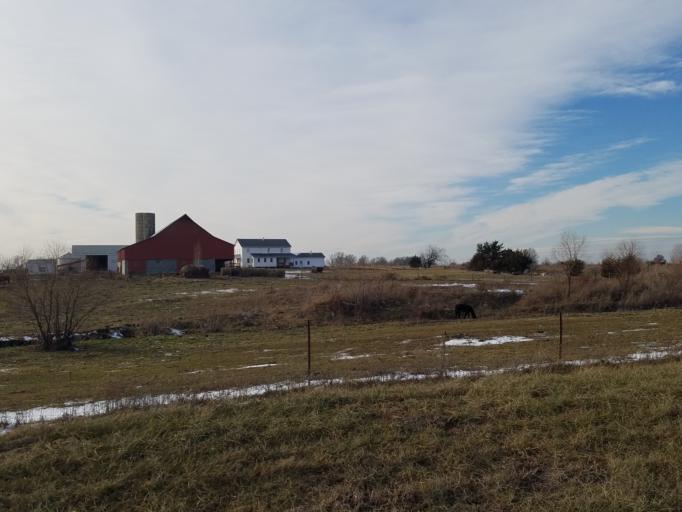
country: US
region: Missouri
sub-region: Boone County
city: Centralia
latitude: 39.2791
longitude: -92.2862
